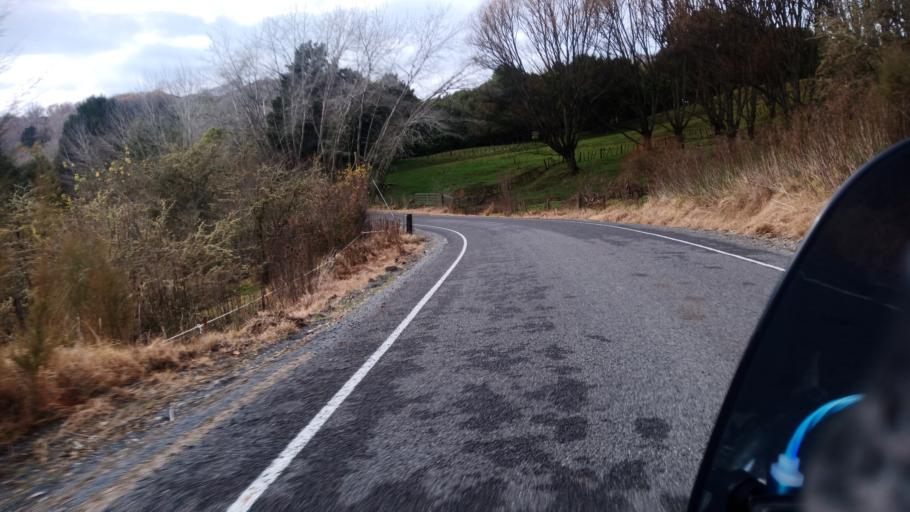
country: NZ
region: Gisborne
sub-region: Gisborne District
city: Gisborne
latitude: -38.4106
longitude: 177.9361
